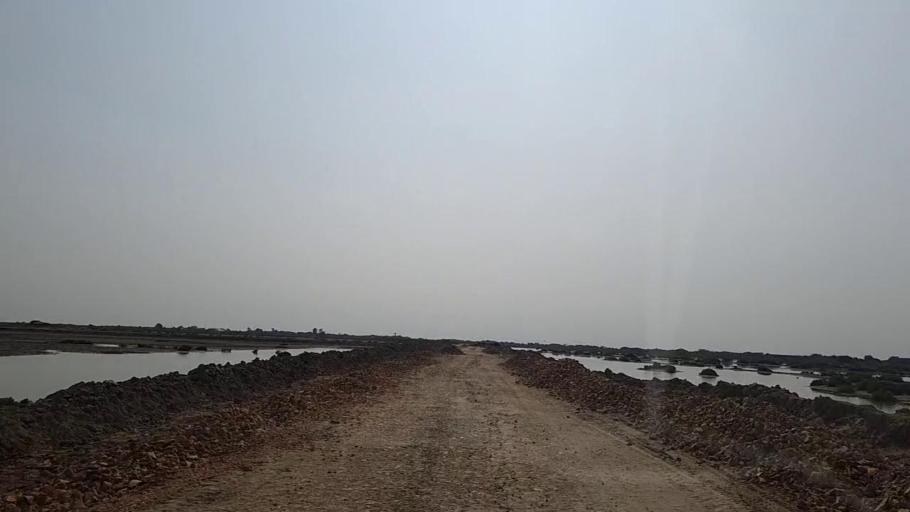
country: PK
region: Sindh
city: Chuhar Jamali
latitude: 24.1989
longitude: 67.8493
